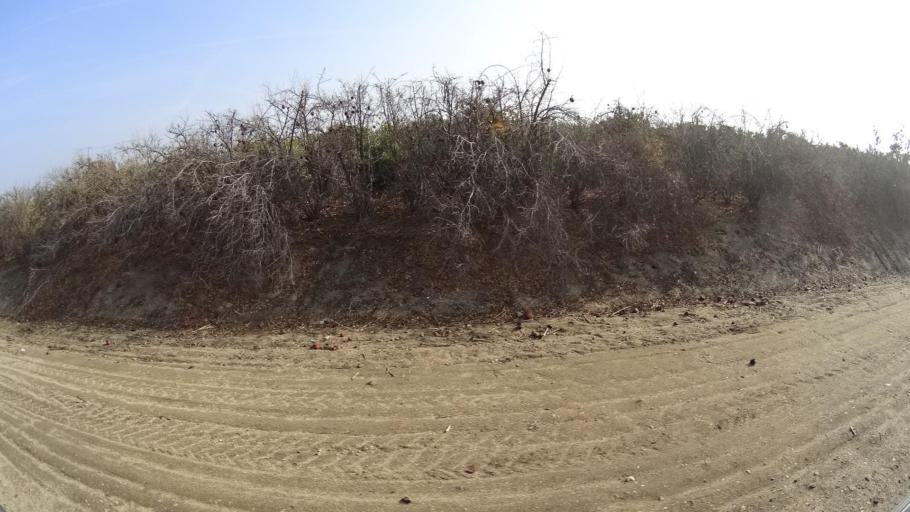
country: US
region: California
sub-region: Kern County
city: Arvin
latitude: 35.0254
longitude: -118.8466
